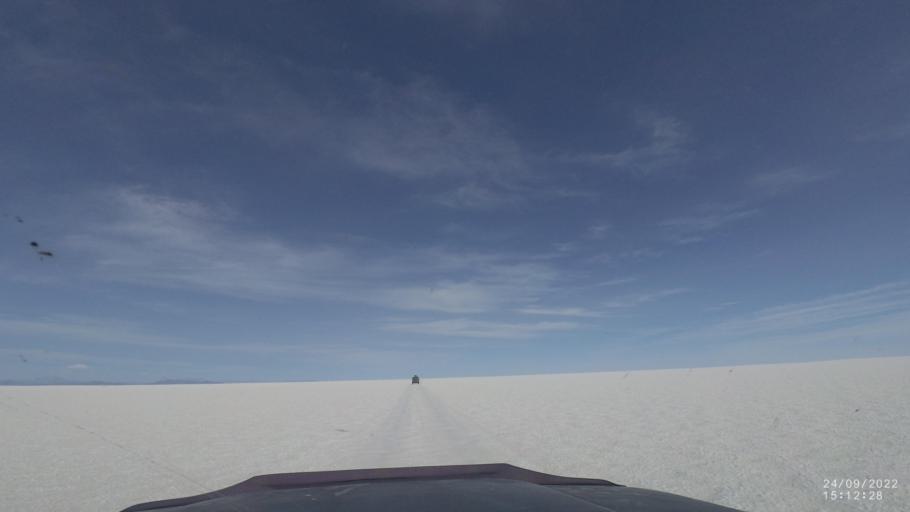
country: BO
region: Potosi
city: Colchani
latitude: -19.9506
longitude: -67.4706
